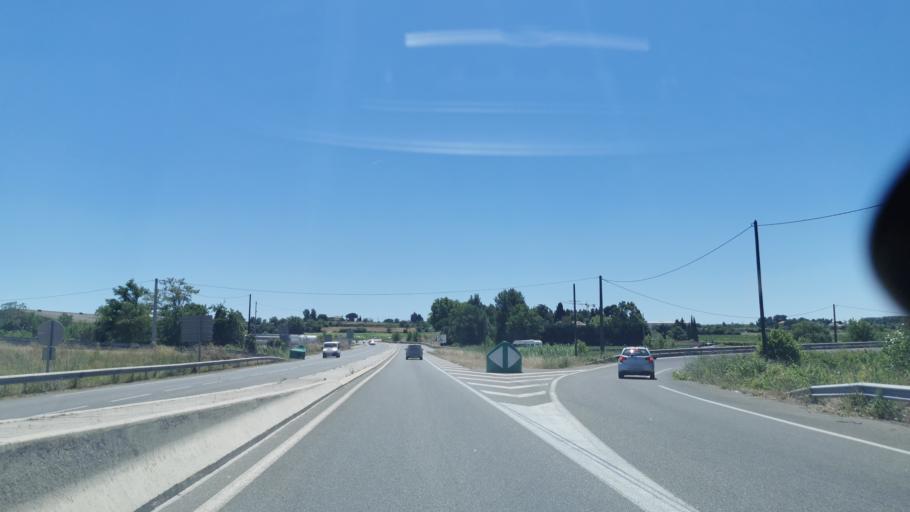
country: FR
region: Languedoc-Roussillon
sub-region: Departement de l'Herault
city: Beziers
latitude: 43.3261
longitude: 3.1914
